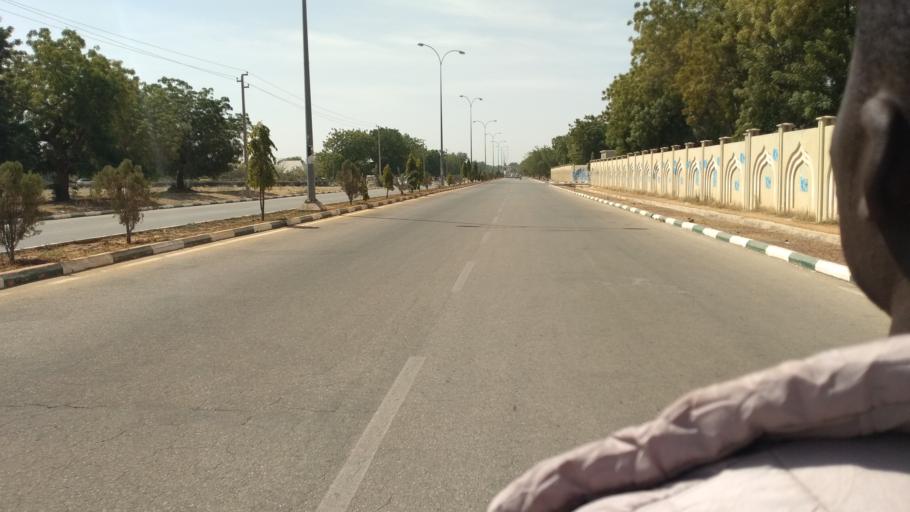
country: NG
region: Jigawa
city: Dutse
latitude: 11.6845
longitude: 9.3364
